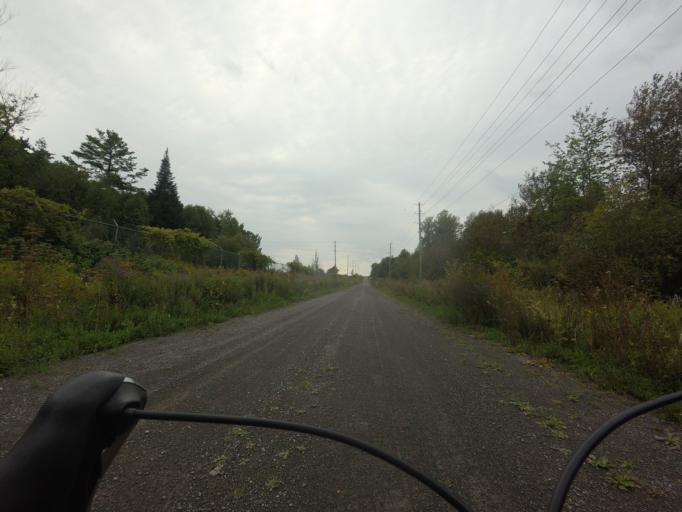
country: CA
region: Ontario
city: Bells Corners
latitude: 45.2403
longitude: -75.7683
